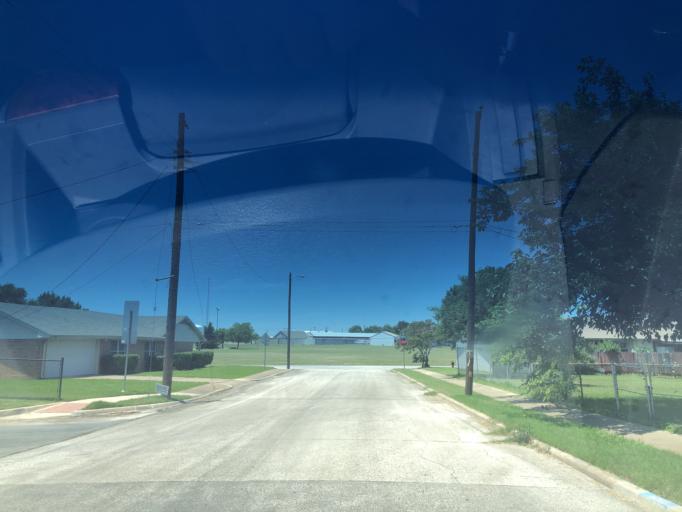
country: US
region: Texas
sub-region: Dallas County
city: Grand Prairie
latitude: 32.7182
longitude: -97.0119
